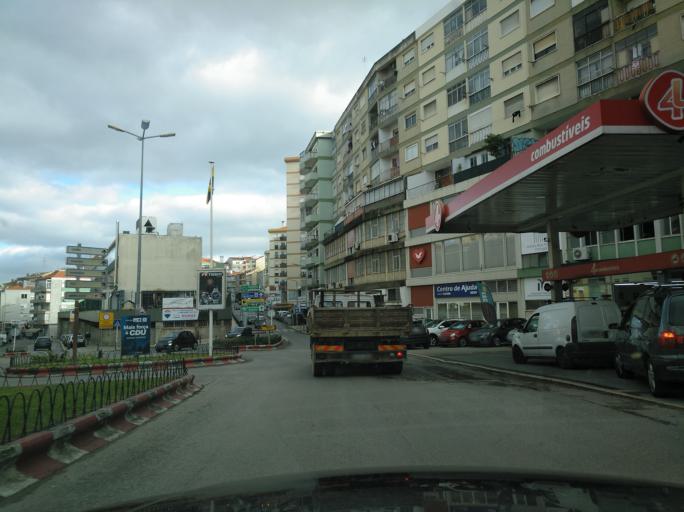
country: PT
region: Lisbon
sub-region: Loures
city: Sacavem
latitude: 38.7937
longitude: -9.1099
